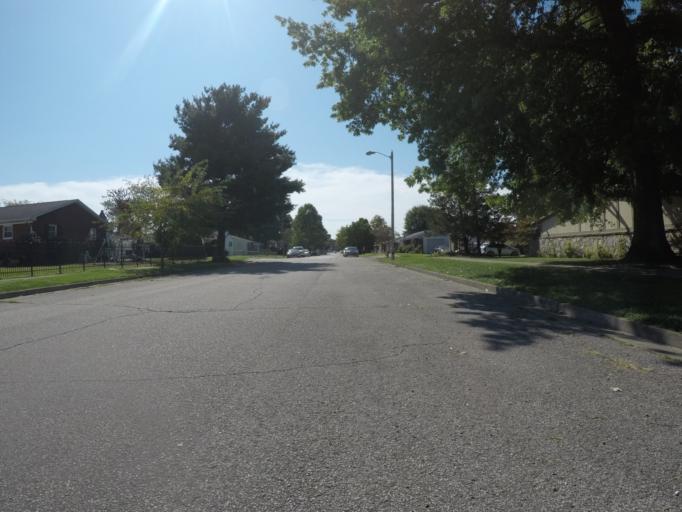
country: US
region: Ohio
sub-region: Lawrence County
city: Ironton
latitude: 38.5389
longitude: -82.6869
